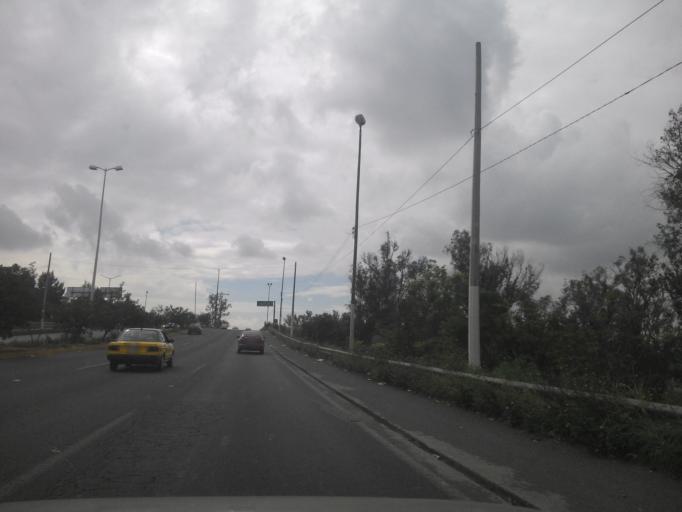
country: MX
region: Jalisco
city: Zapopan2
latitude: 20.6974
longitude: -103.4565
